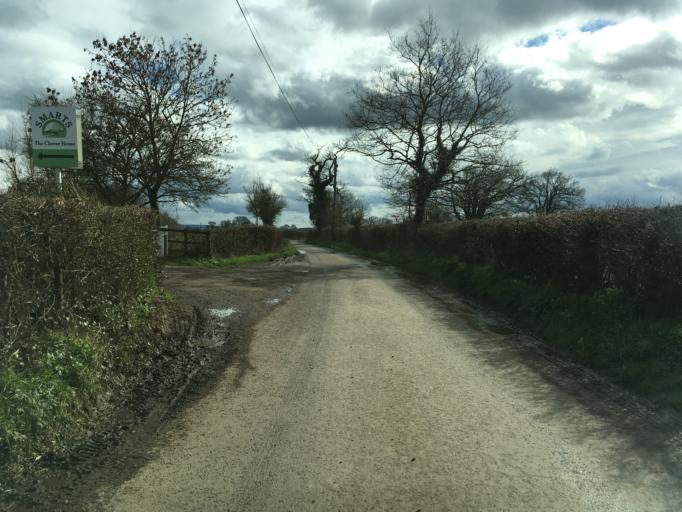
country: GB
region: England
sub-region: Gloucestershire
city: Newent
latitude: 51.8586
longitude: -2.3816
